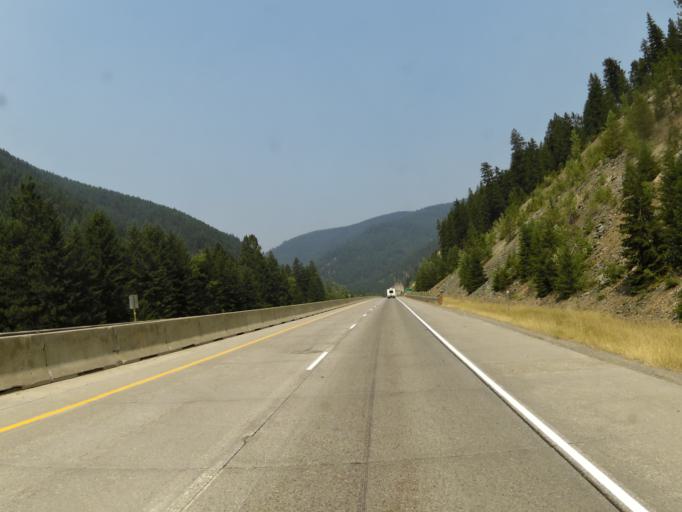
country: US
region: Montana
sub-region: Sanders County
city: Thompson Falls
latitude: 47.3027
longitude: -115.2012
